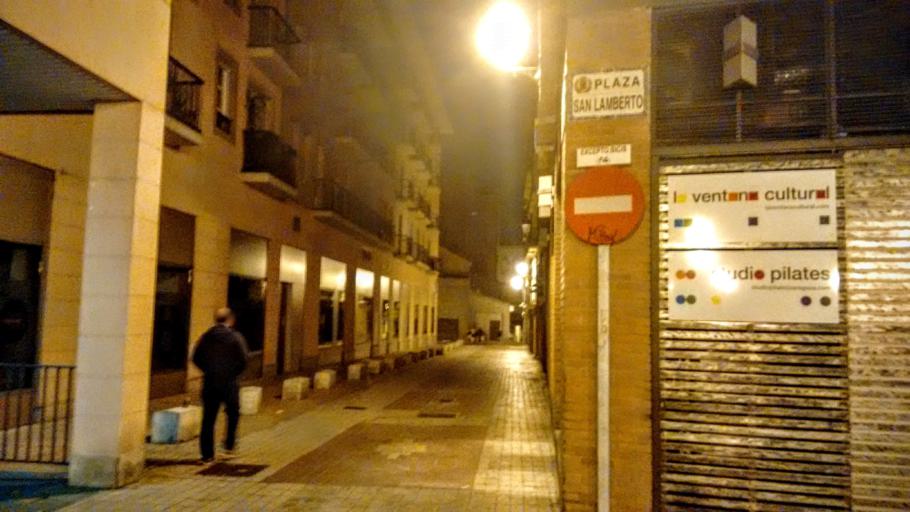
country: ES
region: Aragon
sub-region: Provincia de Zaragoza
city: Zaragoza
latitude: 41.6533
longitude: -0.8855
